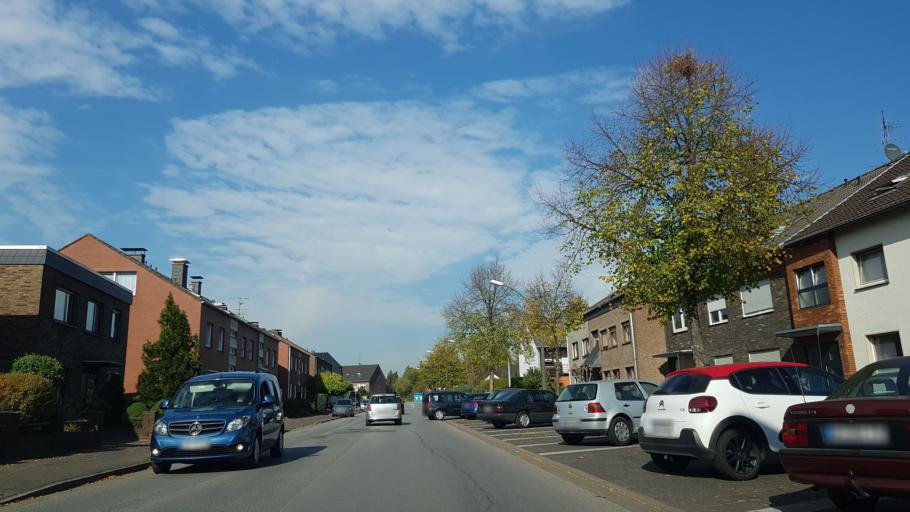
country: DE
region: North Rhine-Westphalia
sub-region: Regierungsbezirk Dusseldorf
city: Moers
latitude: 51.4179
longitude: 6.6727
